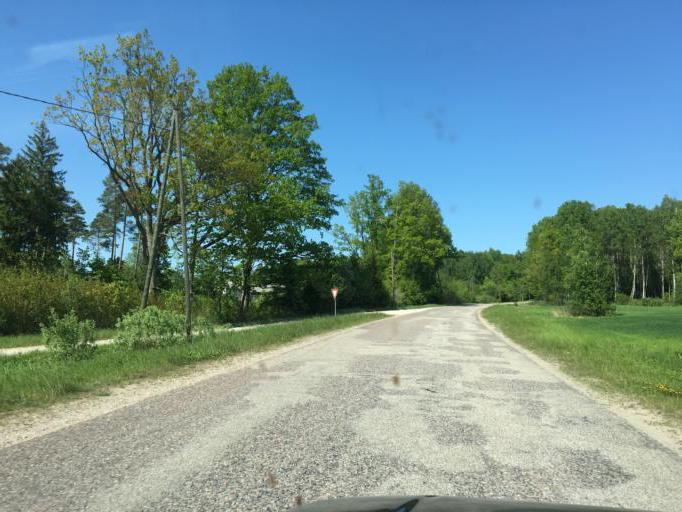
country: LV
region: Dundaga
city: Dundaga
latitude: 57.4939
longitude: 22.3444
